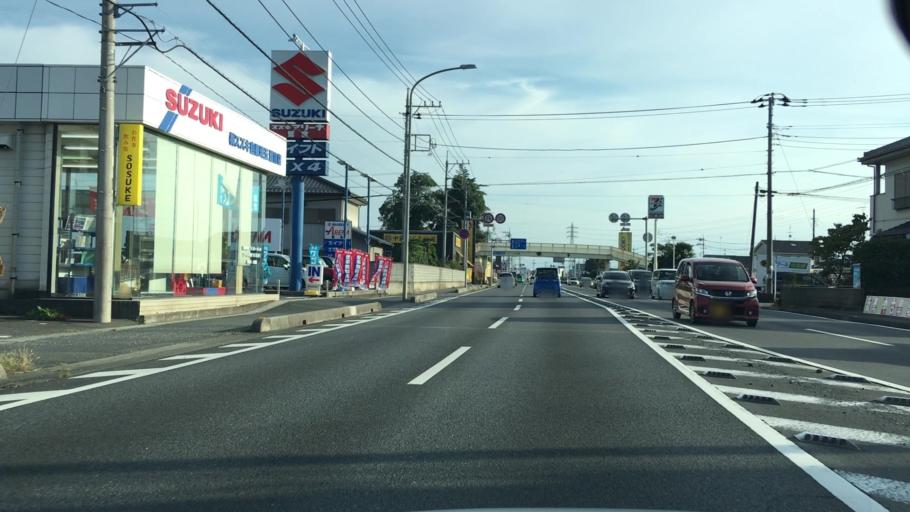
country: JP
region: Saitama
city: Kukichuo
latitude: 36.0934
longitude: 139.6757
